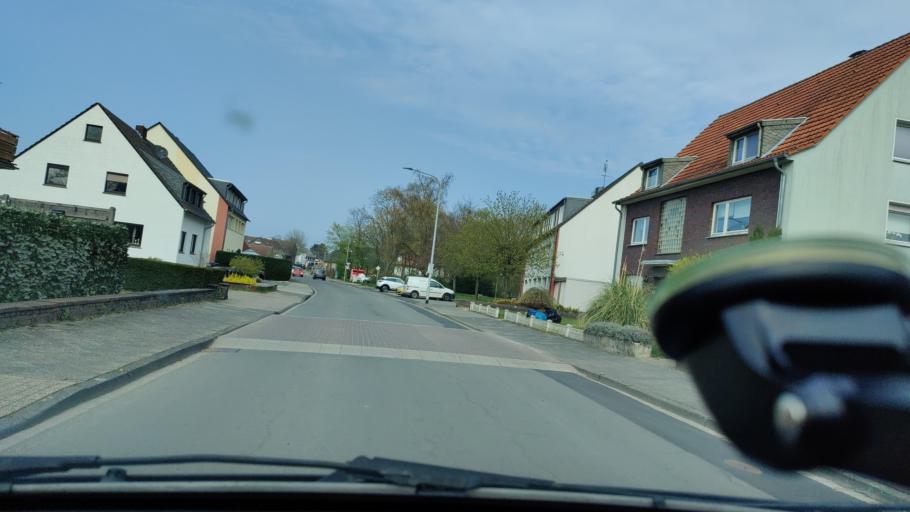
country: DE
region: North Rhine-Westphalia
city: Rheinberg
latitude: 51.5302
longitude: 6.6370
